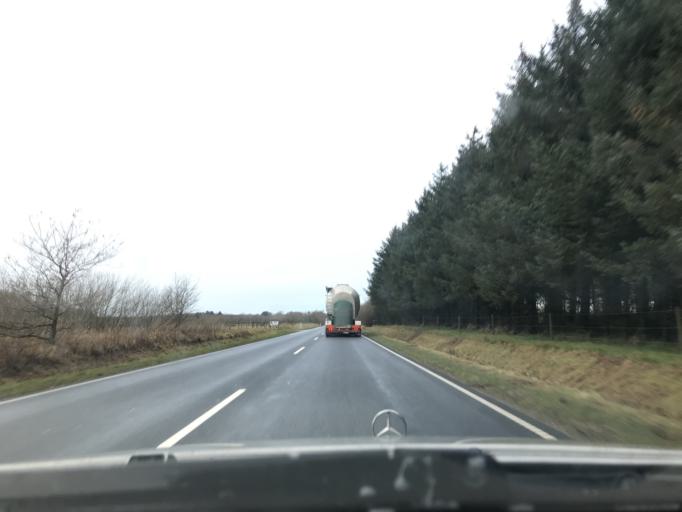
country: DK
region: South Denmark
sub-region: Esbjerg Kommune
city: Ribe
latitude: 55.3084
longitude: 8.7973
